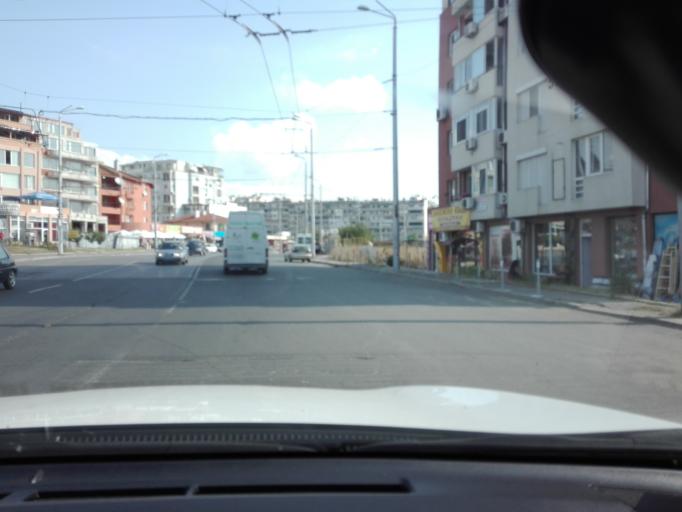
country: BG
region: Burgas
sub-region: Obshtina Burgas
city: Burgas
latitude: 42.4518
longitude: 27.4191
